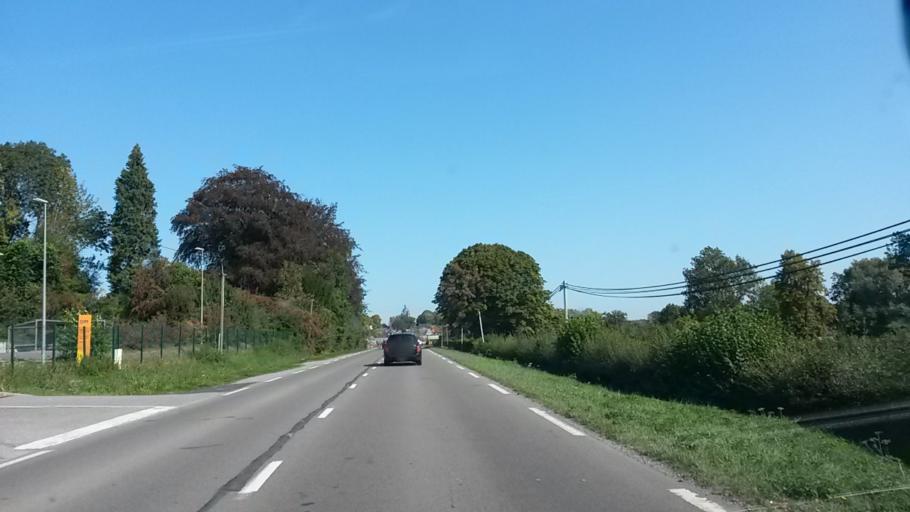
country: FR
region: Nord-Pas-de-Calais
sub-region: Departement du Nord
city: Avesnes-sur-Helpe
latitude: 50.1114
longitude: 3.9318
